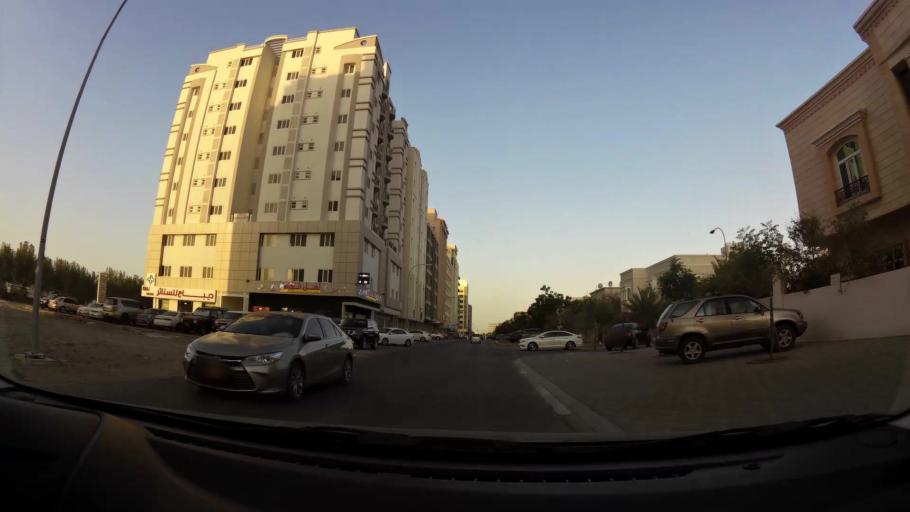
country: OM
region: Muhafazat Masqat
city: As Sib al Jadidah
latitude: 23.6147
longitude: 58.2031
